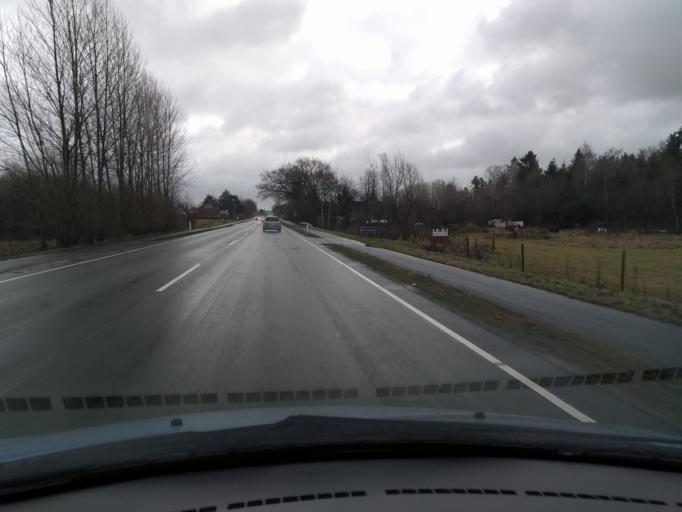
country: DK
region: South Denmark
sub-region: Kerteminde Kommune
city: Langeskov
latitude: 55.3723
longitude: 10.5620
